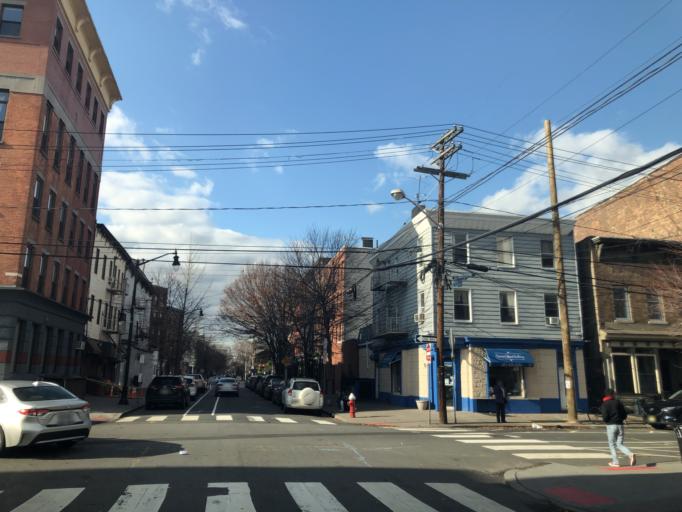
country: US
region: New Jersey
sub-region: Hudson County
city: Hoboken
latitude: 40.7228
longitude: -74.0473
